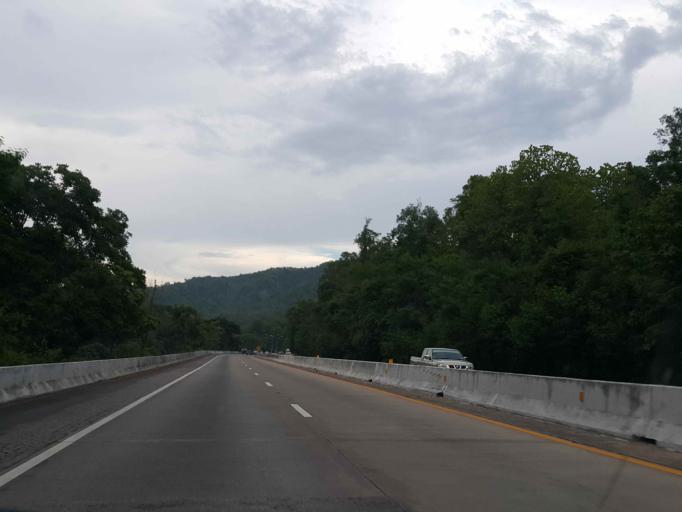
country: TH
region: Lampang
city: Hang Chat
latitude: 18.3668
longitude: 99.2369
